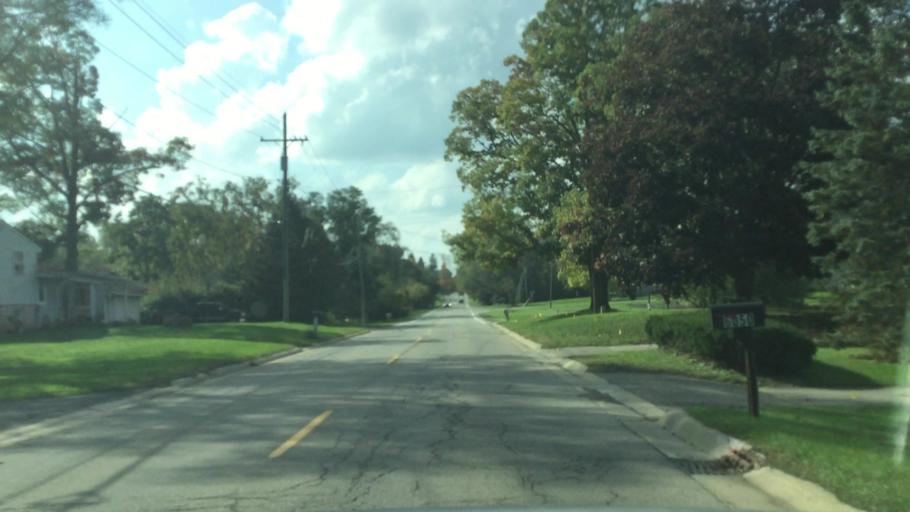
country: US
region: Michigan
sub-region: Oakland County
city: Waterford
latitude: 42.6525
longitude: -83.4083
